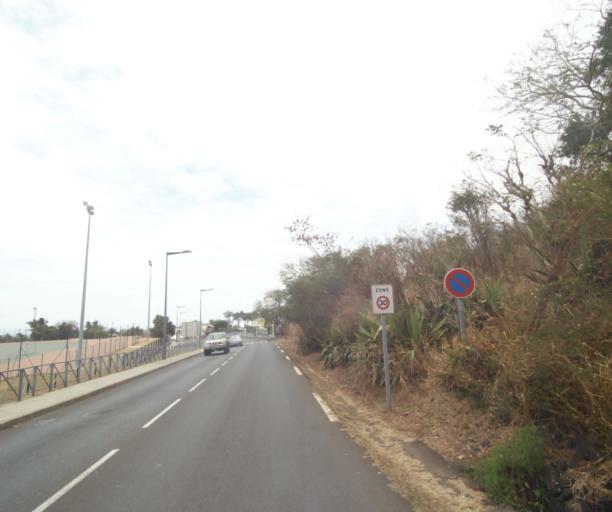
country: RE
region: Reunion
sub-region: Reunion
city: Saint-Paul
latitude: -21.0300
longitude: 55.2704
